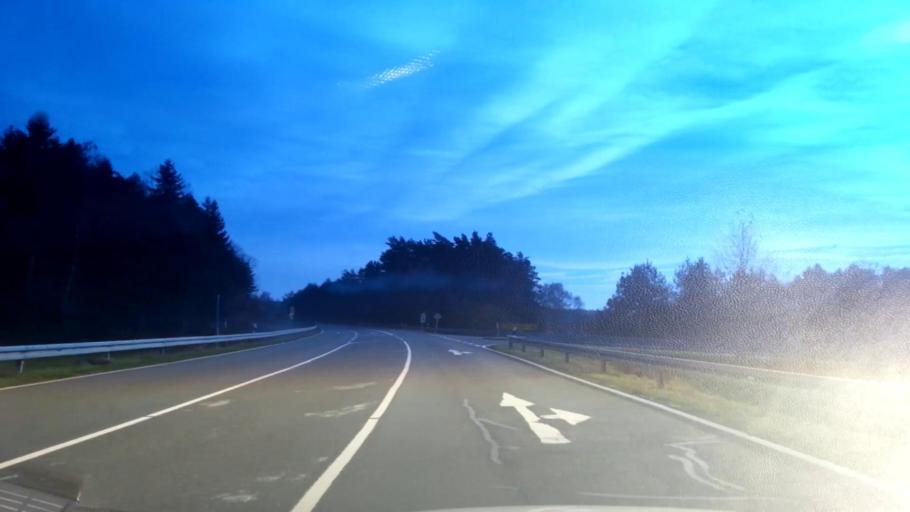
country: DE
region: Bavaria
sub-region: Upper Franconia
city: Kirchenpingarten
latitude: 49.9222
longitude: 11.7958
